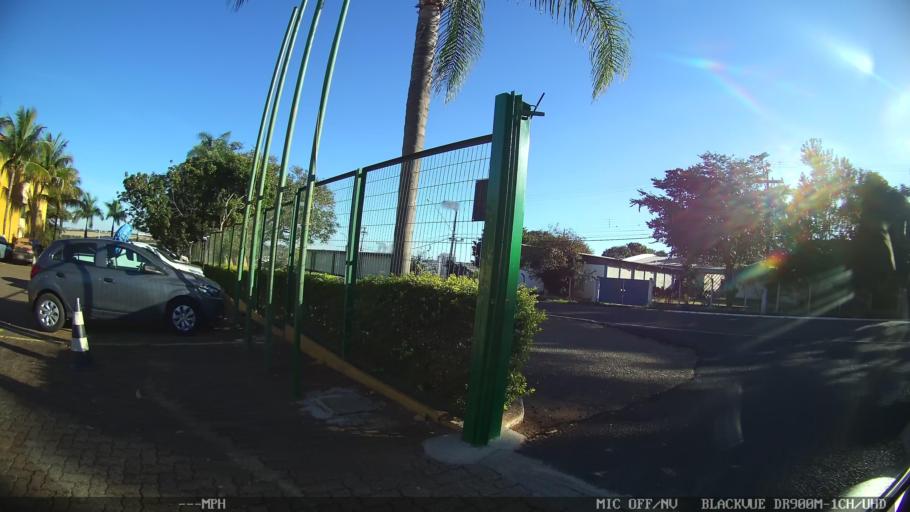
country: BR
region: Sao Paulo
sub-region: Franca
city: Franca
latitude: -20.5623
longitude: -47.4097
